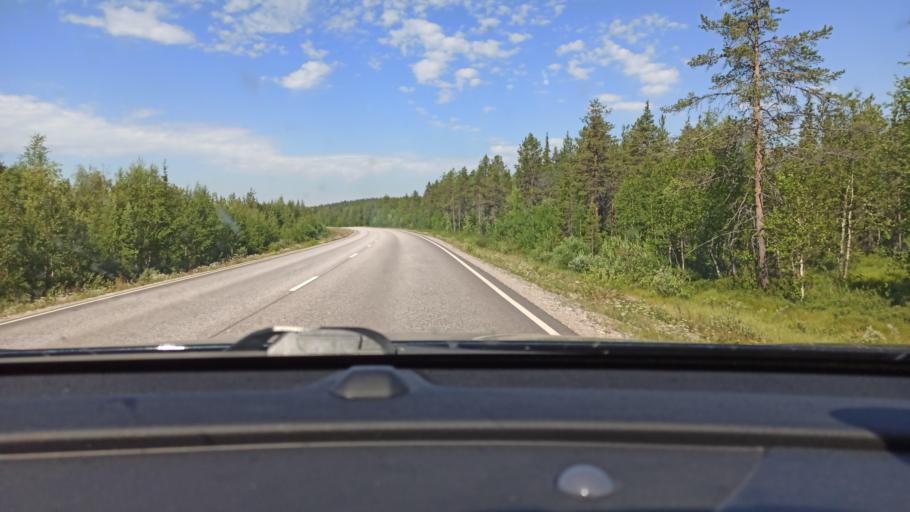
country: FI
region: Lapland
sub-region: Tunturi-Lappi
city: Muonio
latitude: 67.9886
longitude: 23.6406
